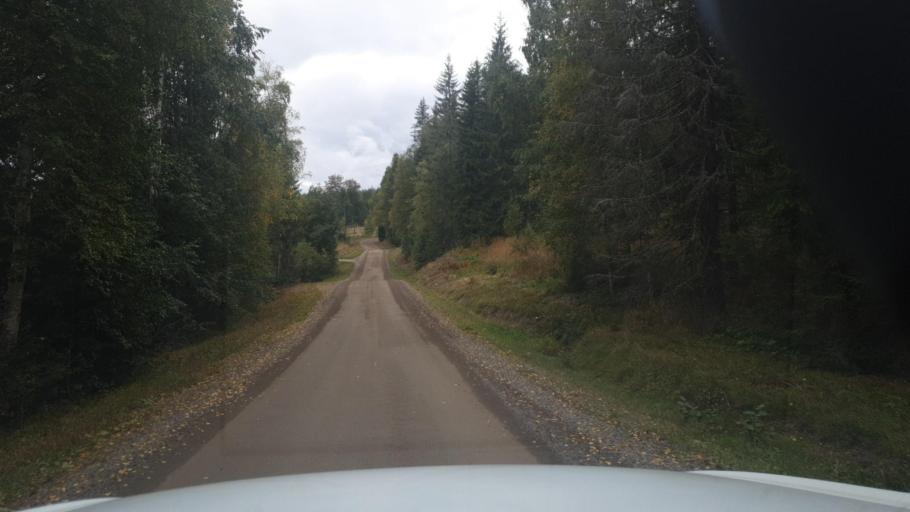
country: SE
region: Vaermland
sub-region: Sunne Kommun
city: Sunne
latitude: 59.8234
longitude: 12.8842
